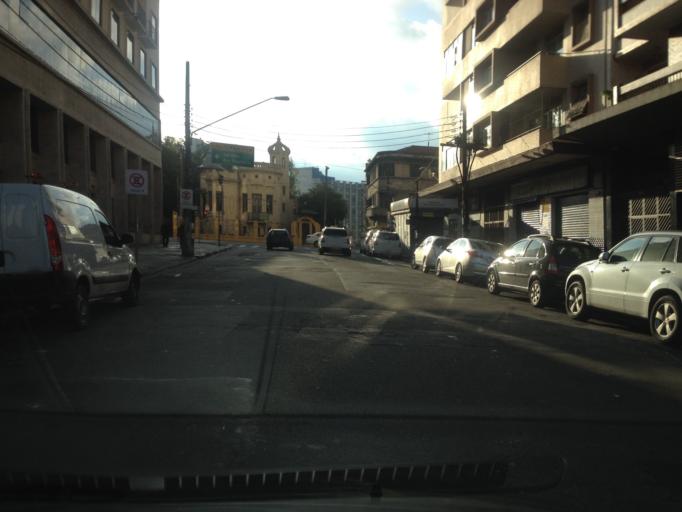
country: BR
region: Sao Paulo
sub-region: Sao Paulo
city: Sao Paulo
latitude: -23.5576
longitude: -46.6401
